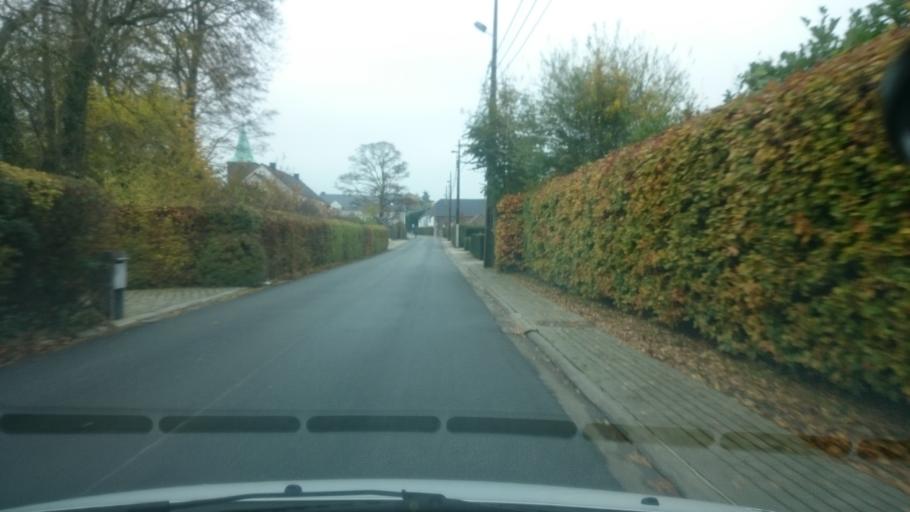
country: BE
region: Wallonia
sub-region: Province du Brabant Wallon
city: Walhain-Saint-Paul
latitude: 50.6419
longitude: 4.6775
